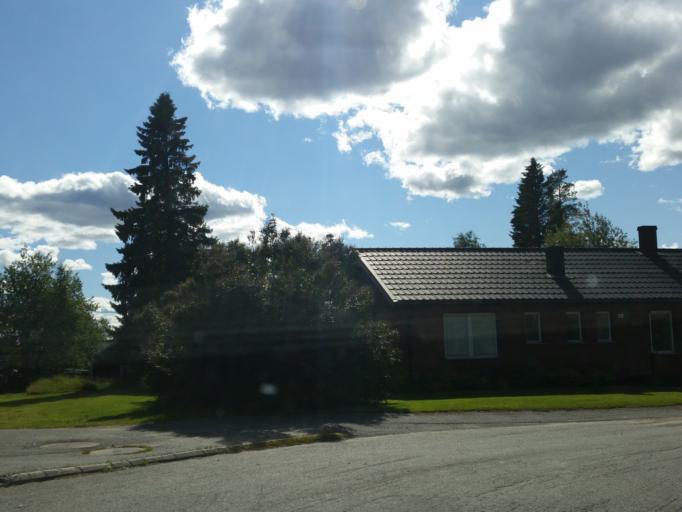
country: SE
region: Vaesterbotten
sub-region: Robertsfors Kommun
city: Robertsfors
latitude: 64.1976
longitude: 20.8443
